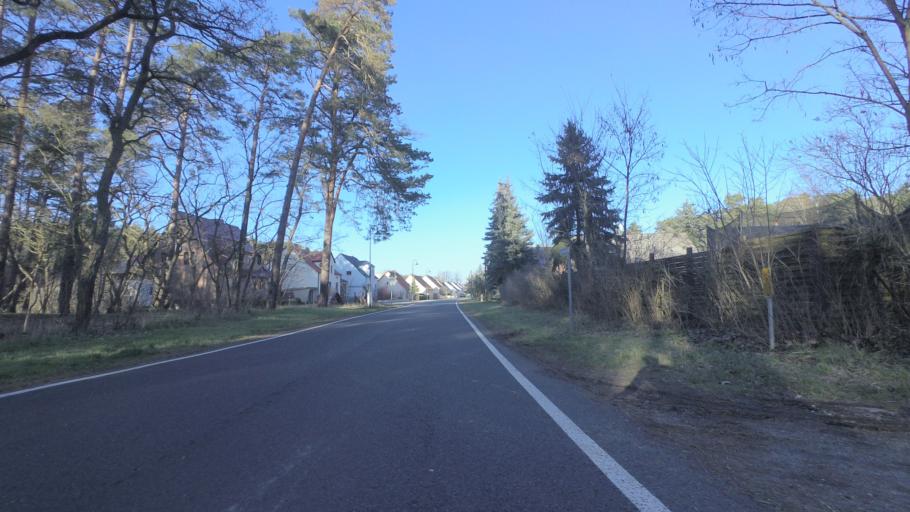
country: DE
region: Brandenburg
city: Sperenberg
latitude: 52.0391
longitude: 13.3193
